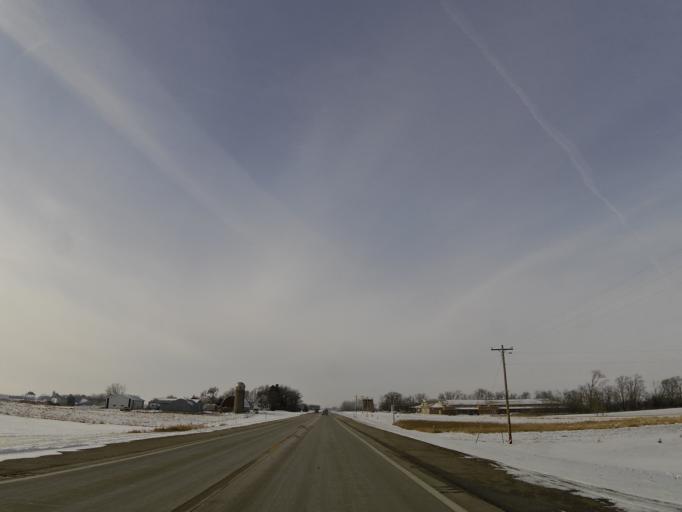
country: US
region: Minnesota
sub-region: McLeod County
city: Hutchinson
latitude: 44.8926
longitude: -94.2889
